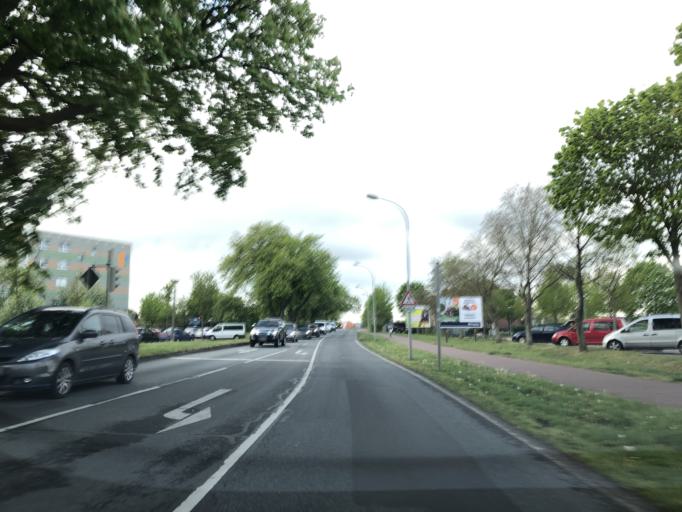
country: DE
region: Mecklenburg-Vorpommern
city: Guestrow
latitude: 53.7775
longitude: 12.1731
